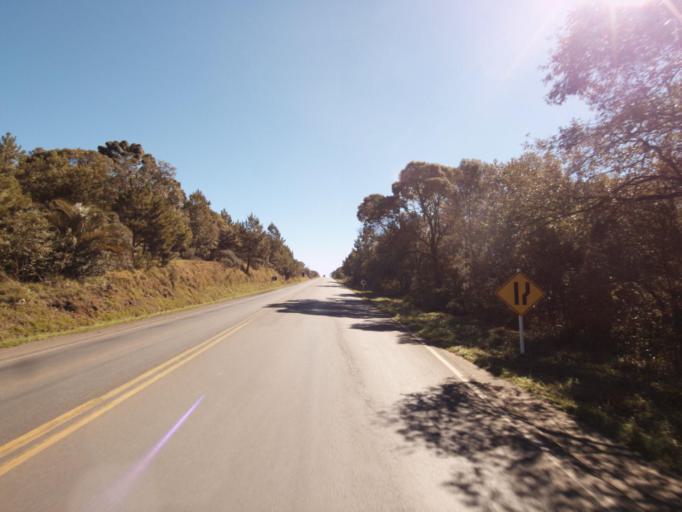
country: BR
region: Santa Catarina
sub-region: Concordia
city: Concordia
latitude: -26.9194
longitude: -51.9546
